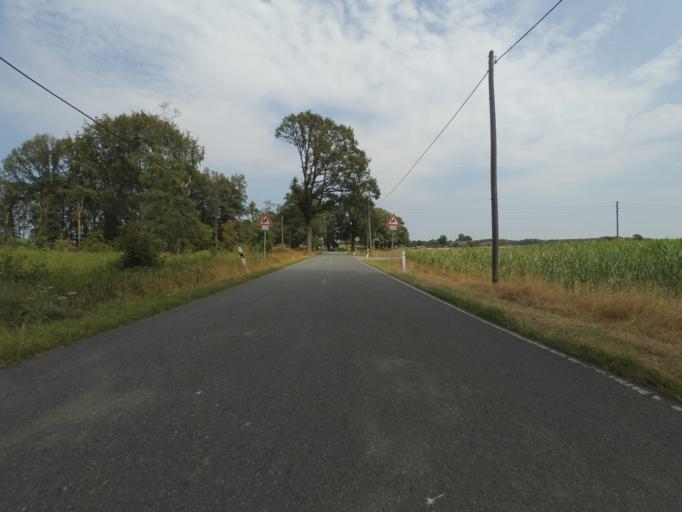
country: DE
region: North Rhine-Westphalia
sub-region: Regierungsbezirk Munster
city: Isselburg
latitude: 51.7885
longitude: 6.4690
